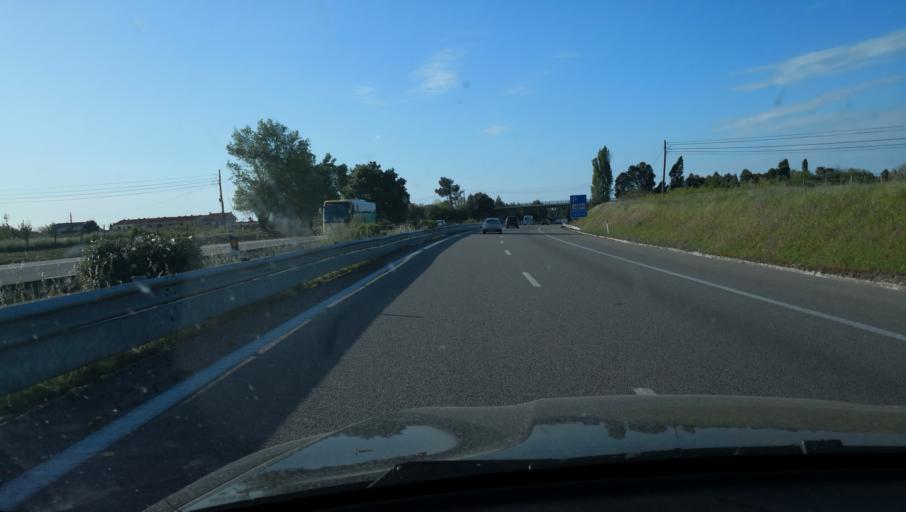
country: PT
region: Aveiro
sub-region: Oliveira do Bairro
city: Oia
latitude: 40.5395
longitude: -8.5606
